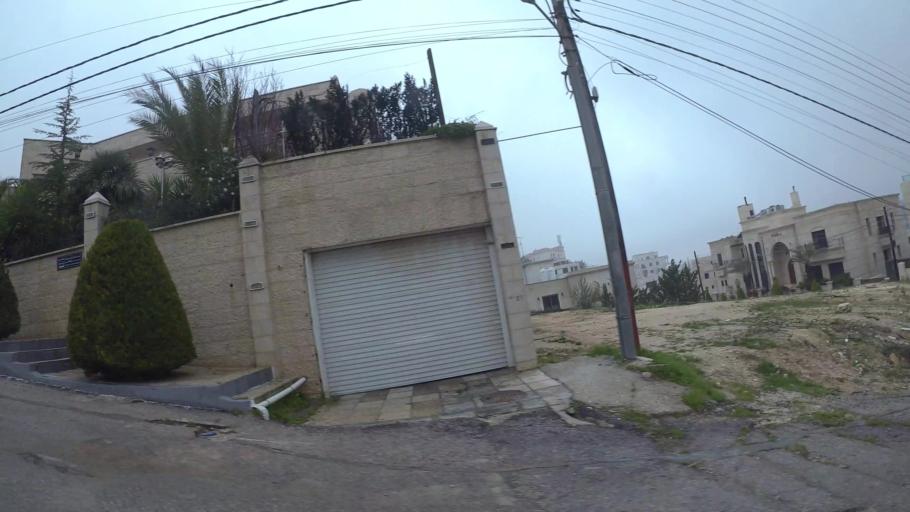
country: JO
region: Amman
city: Al Jubayhah
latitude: 32.0026
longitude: 35.8202
